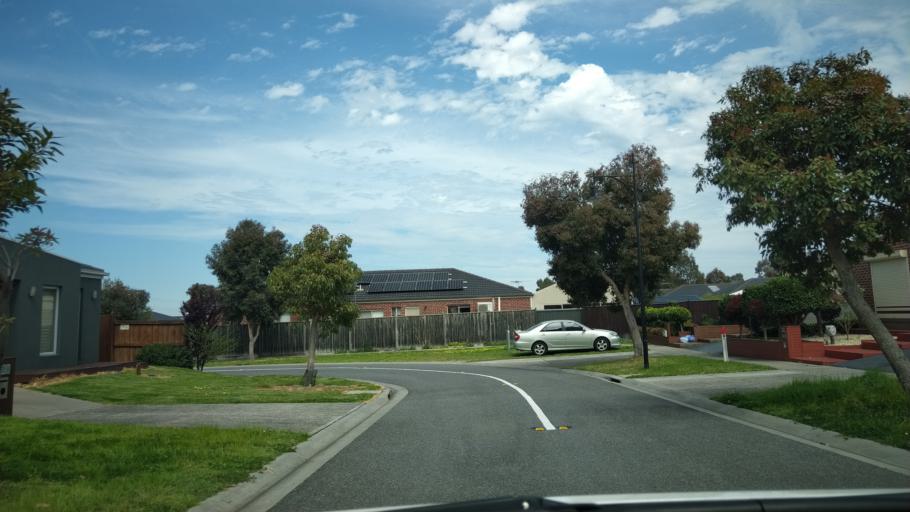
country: AU
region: Victoria
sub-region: Greater Dandenong
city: Keysborough
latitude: -38.0021
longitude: 145.1606
